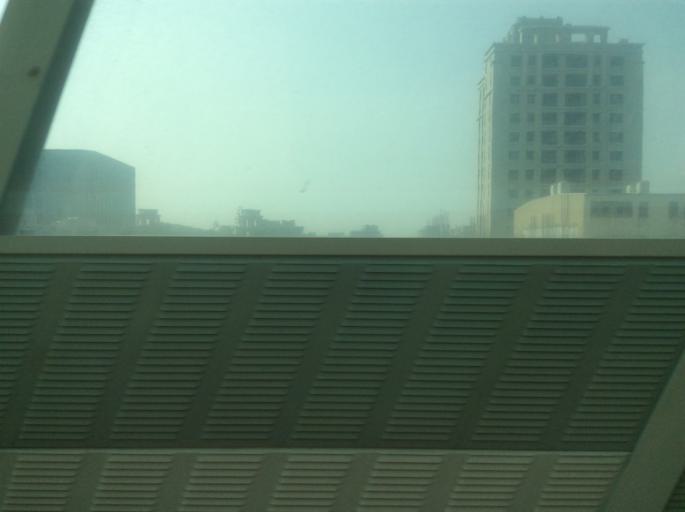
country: TW
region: Taiwan
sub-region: Nantou
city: Nantou
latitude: 23.9633
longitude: 120.5692
